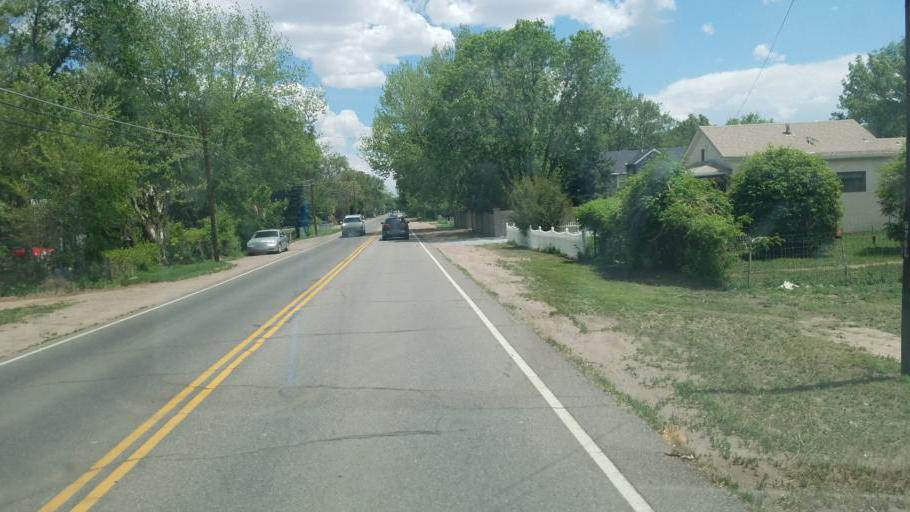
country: US
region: Colorado
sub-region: Fremont County
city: Florence
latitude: 38.4006
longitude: -105.1344
